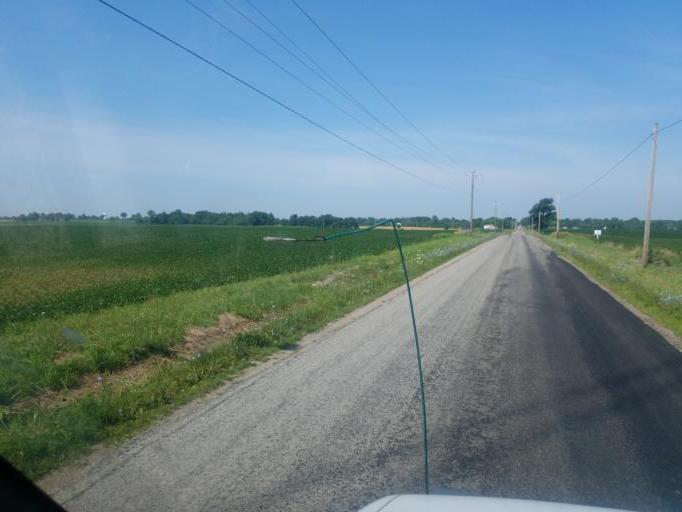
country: US
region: Ohio
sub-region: Union County
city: Marysville
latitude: 40.2900
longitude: -83.3322
